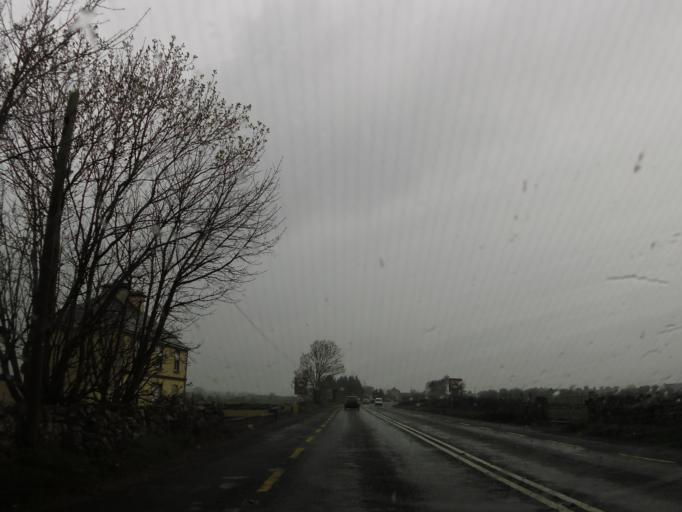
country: IE
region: Connaught
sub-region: County Galway
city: Tuam
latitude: 53.4922
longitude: -8.8994
